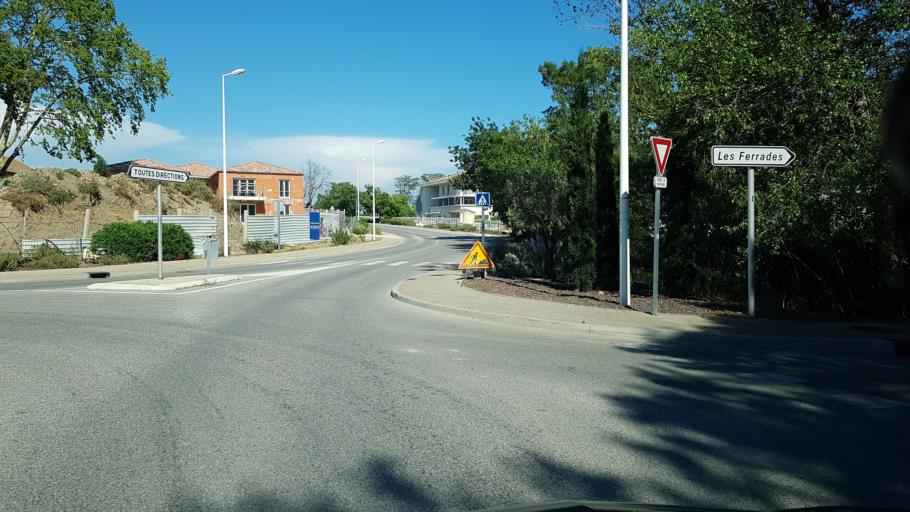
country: FR
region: Provence-Alpes-Cote d'Azur
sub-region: Departement des Bouches-du-Rhone
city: Saint-Martin-de-Crau
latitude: 43.6330
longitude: 4.8119
